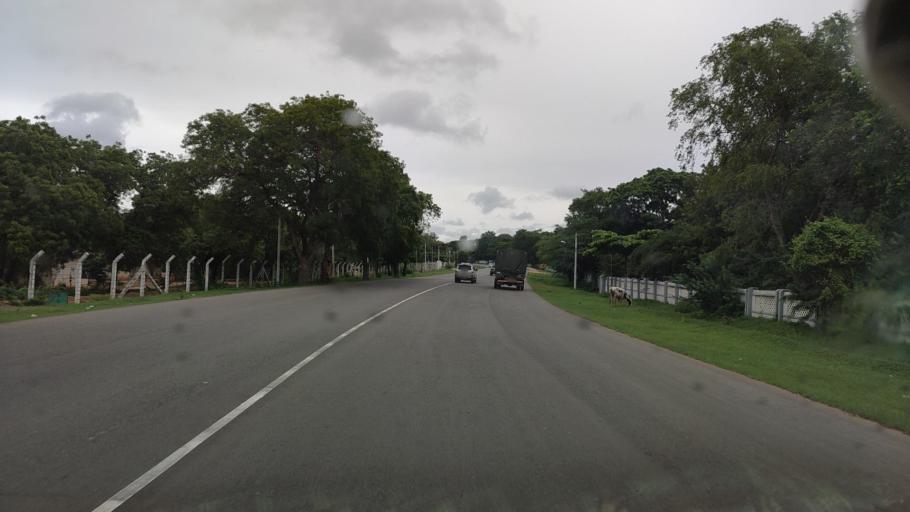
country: MM
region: Mandalay
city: Meiktila
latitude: 20.8399
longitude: 95.8940
